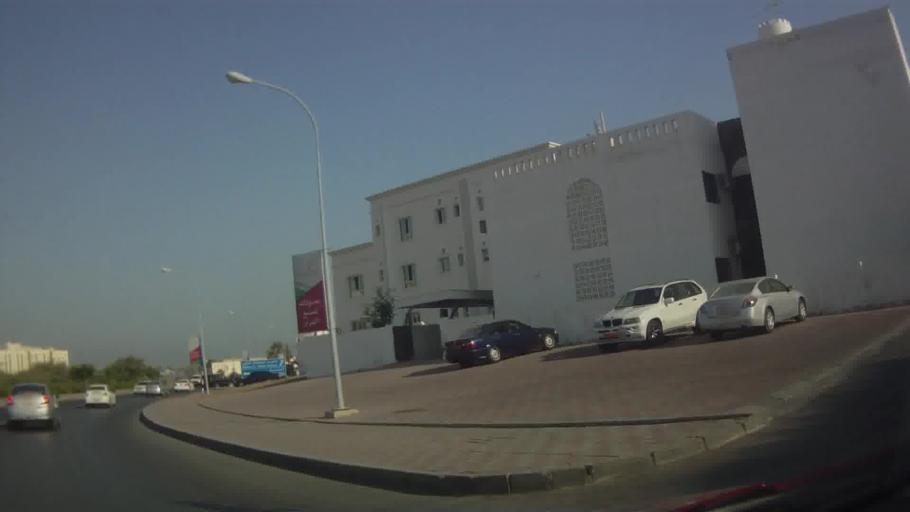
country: OM
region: Muhafazat Masqat
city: Bawshar
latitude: 23.5900
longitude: 58.4184
